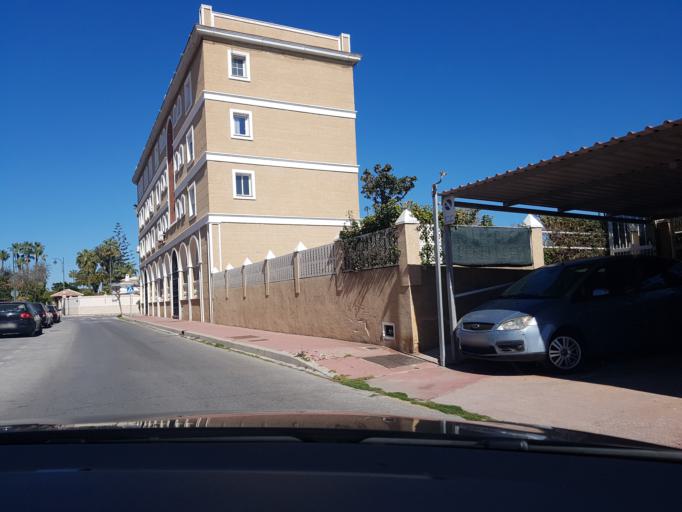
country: ES
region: Andalusia
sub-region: Provincia de Malaga
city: Torremolinos
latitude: 36.6663
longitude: -4.4571
